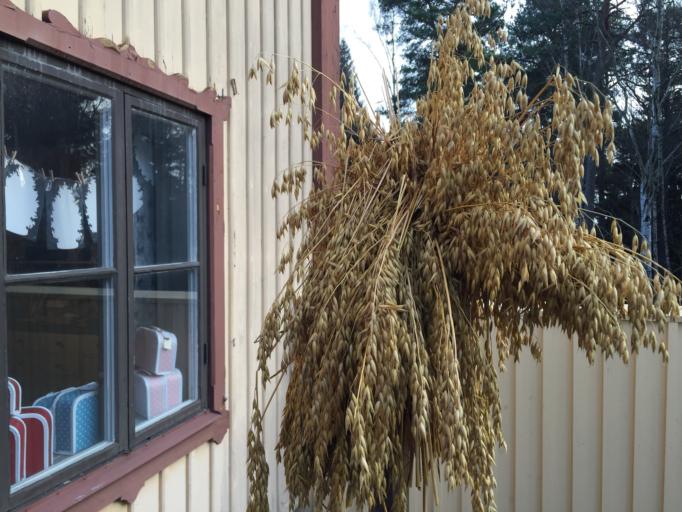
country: SE
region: Stockholm
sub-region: Sodertalje Kommun
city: Soedertaelje
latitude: 59.1910
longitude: 17.6186
